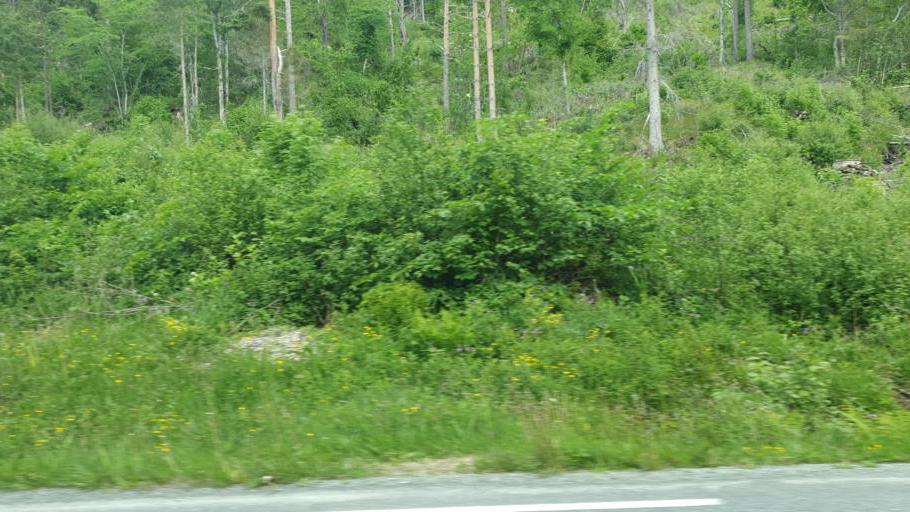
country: NO
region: Sor-Trondelag
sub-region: Trondheim
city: Trondheim
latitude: 63.5571
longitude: 10.2919
